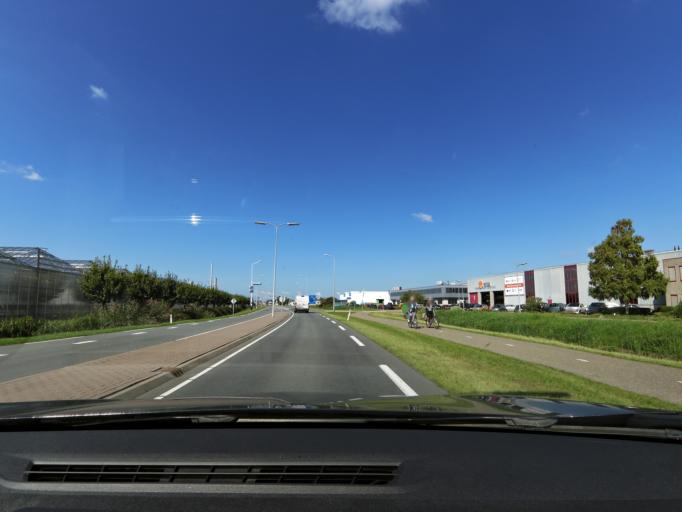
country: NL
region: North Holland
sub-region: Gemeente Aalsmeer
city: Aalsmeer
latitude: 52.2390
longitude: 4.7757
